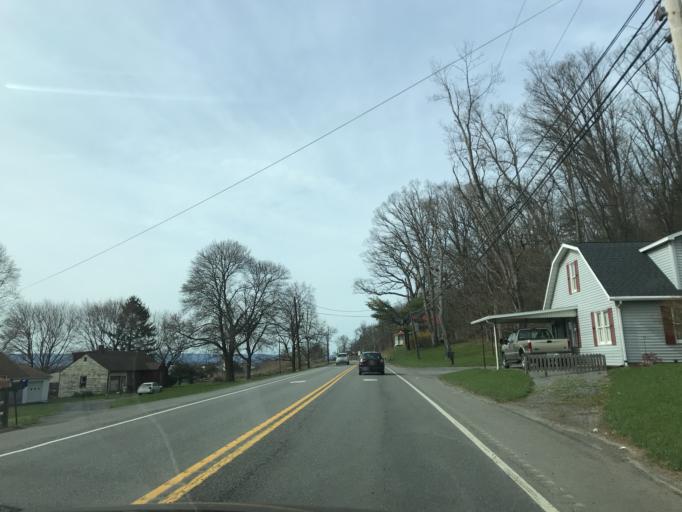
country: US
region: Pennsylvania
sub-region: Union County
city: Lewisburg
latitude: 40.9244
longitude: -76.8455
